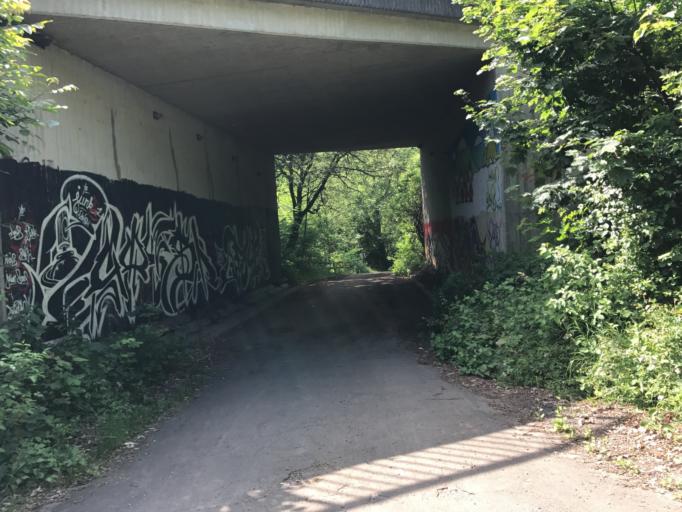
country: DE
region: Hesse
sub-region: Regierungsbezirk Darmstadt
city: Schlangenbad
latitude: 50.0852
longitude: 8.1123
